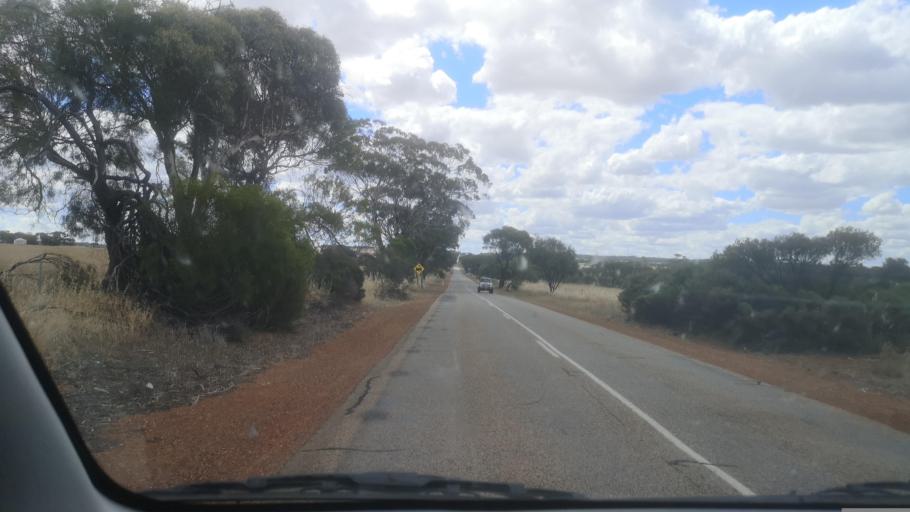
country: AU
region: Western Australia
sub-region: Beverley
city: Beverley
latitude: -31.9824
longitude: 117.0904
